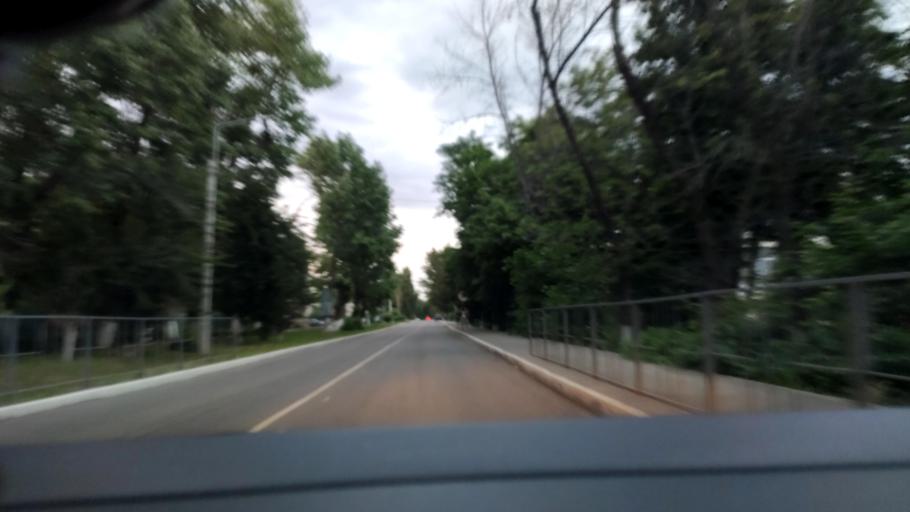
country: RU
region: Voronezj
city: Semiluki
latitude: 51.6927
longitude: 39.0250
